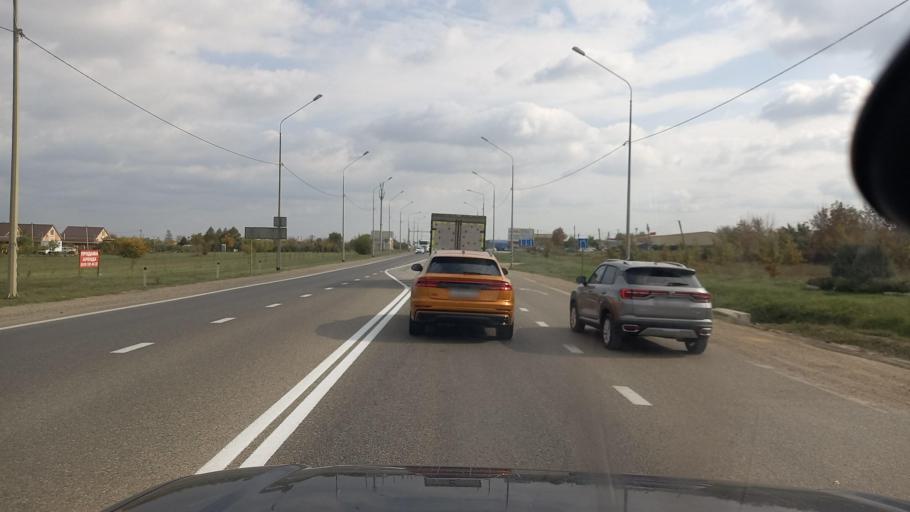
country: RU
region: Krasnodarskiy
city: Il'skiy
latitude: 44.8461
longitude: 38.5505
